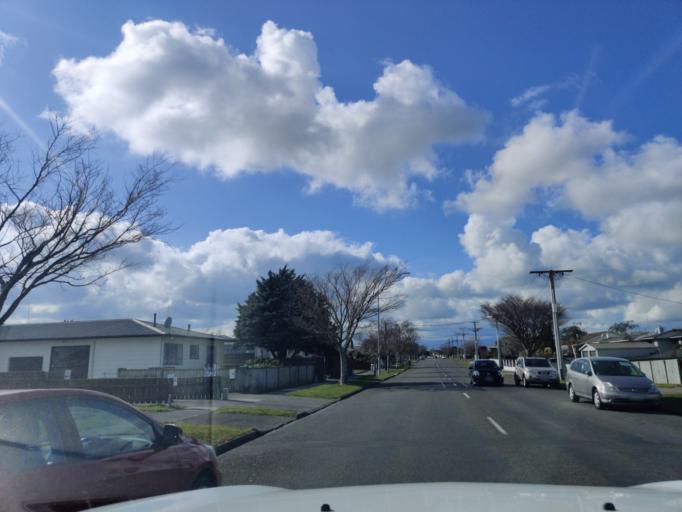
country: NZ
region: Manawatu-Wanganui
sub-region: Palmerston North City
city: Palmerston North
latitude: -40.3358
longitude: 175.6074
